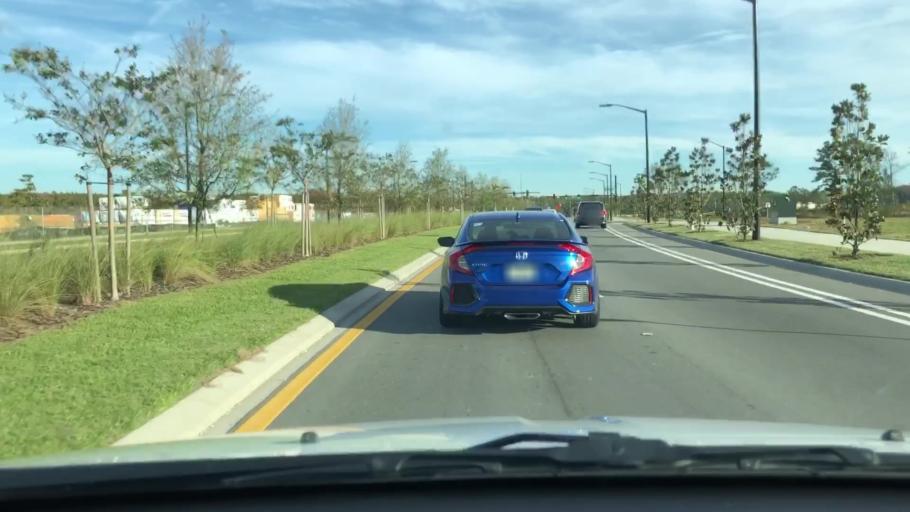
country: US
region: Florida
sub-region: Orange County
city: Hunters Creek
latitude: 28.3431
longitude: -81.3939
